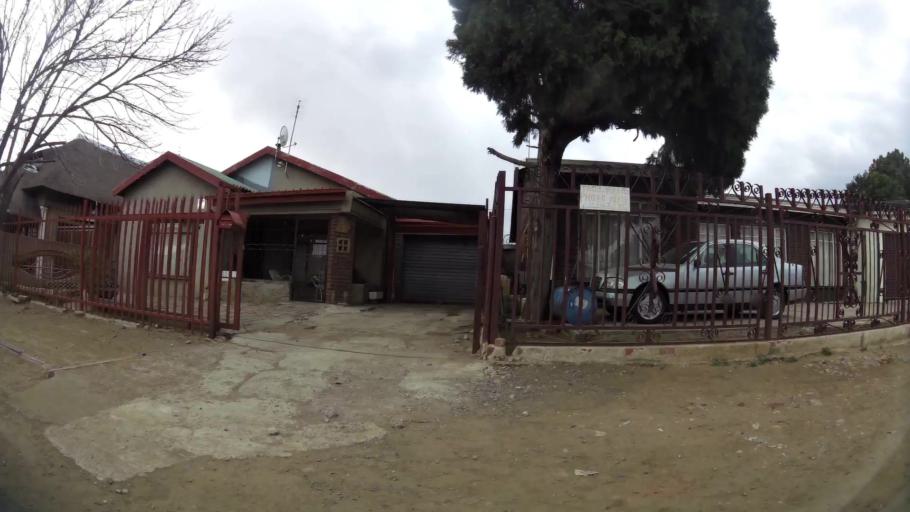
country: ZA
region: Orange Free State
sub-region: Fezile Dabi District Municipality
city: Kroonstad
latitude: -27.6507
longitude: 27.1886
